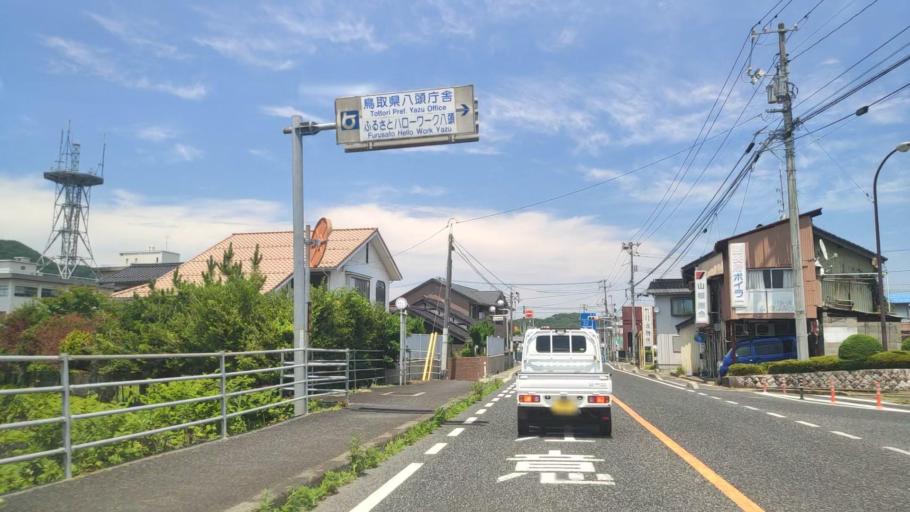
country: JP
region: Tottori
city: Tottori
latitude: 35.4114
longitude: 134.2543
